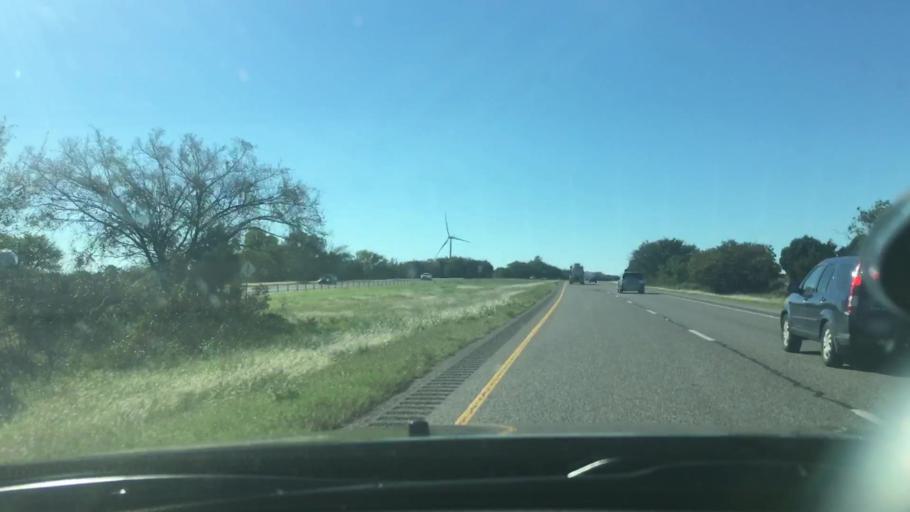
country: US
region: Oklahoma
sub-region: Murray County
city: Davis
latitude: 34.3918
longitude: -97.1421
